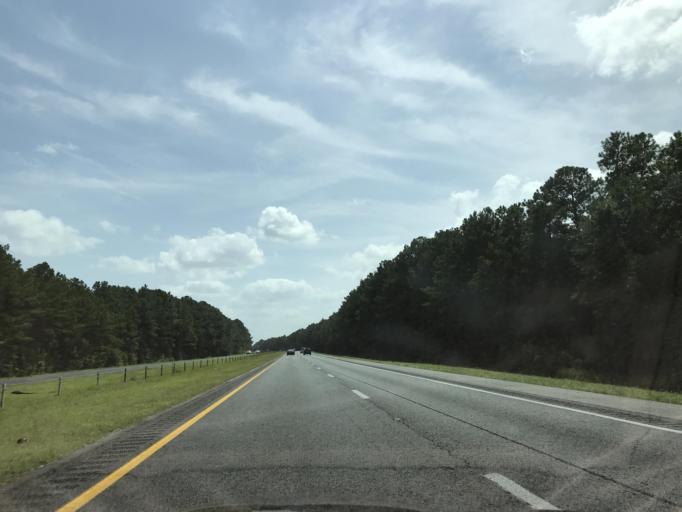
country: US
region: North Carolina
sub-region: Duplin County
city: Wallace
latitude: 34.7129
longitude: -77.9456
